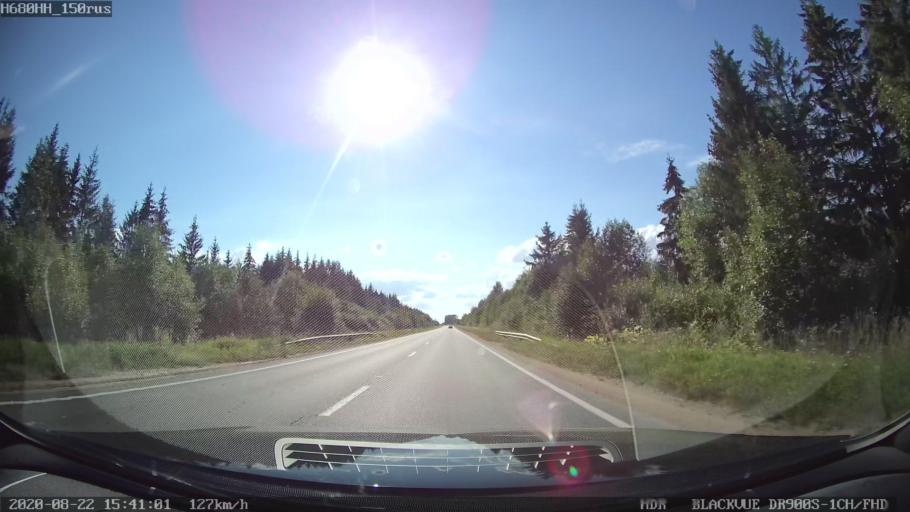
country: RU
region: Tverskaya
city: Bezhetsk
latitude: 57.7515
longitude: 36.5784
